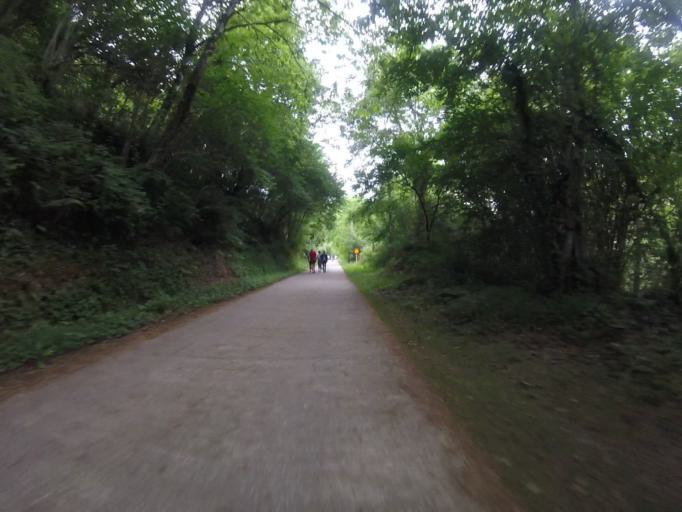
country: ES
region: Navarre
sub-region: Provincia de Navarra
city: Doneztebe
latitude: 43.1479
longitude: -1.6688
